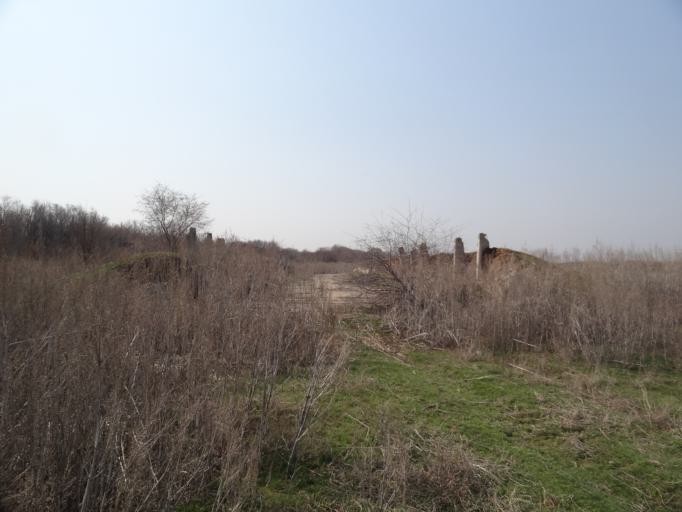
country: RU
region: Saratov
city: Privolzhskiy
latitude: 51.2480
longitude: 45.9337
